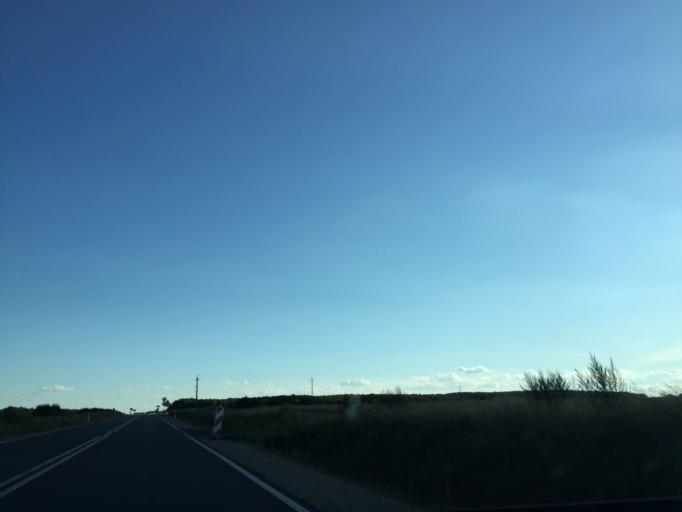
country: PL
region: Podlasie
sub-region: Powiat grajewski
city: Szczuczyn
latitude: 53.4959
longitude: 22.2274
